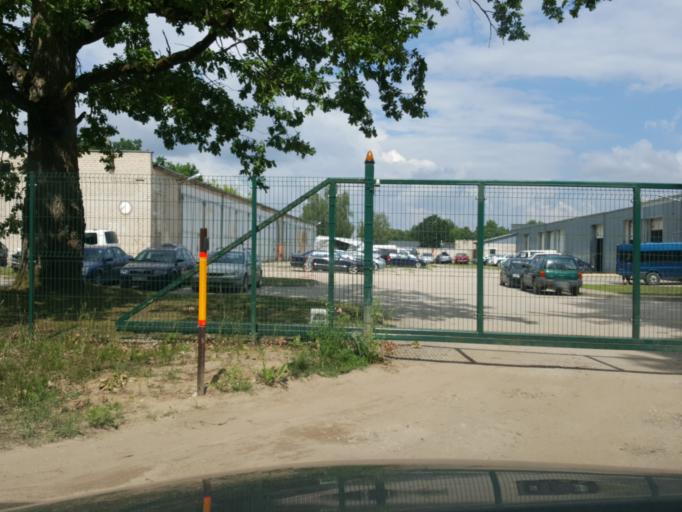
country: LT
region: Alytaus apskritis
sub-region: Alytus
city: Alytus
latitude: 54.3780
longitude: 24.0479
